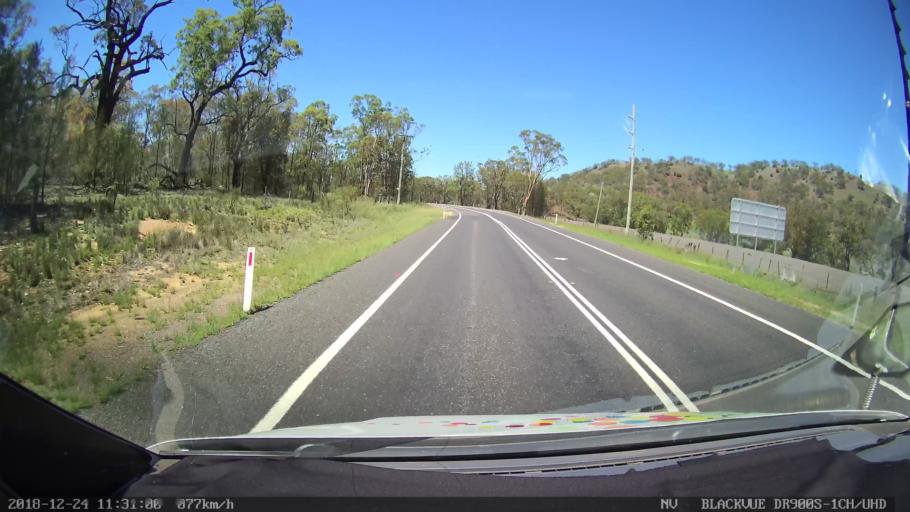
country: AU
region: New South Wales
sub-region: Upper Hunter Shire
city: Merriwa
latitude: -32.2107
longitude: 150.4619
